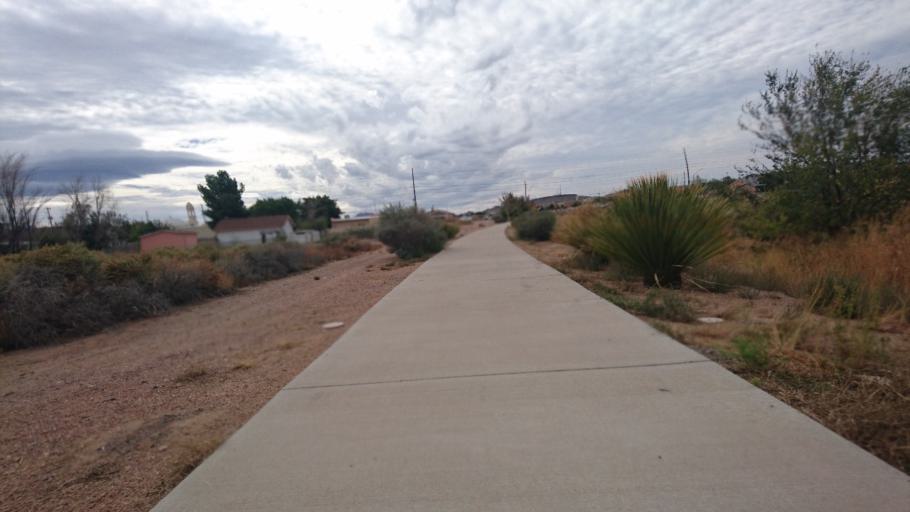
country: US
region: Arizona
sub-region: Mohave County
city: New Kingman-Butler
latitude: 35.2266
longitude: -114.0300
